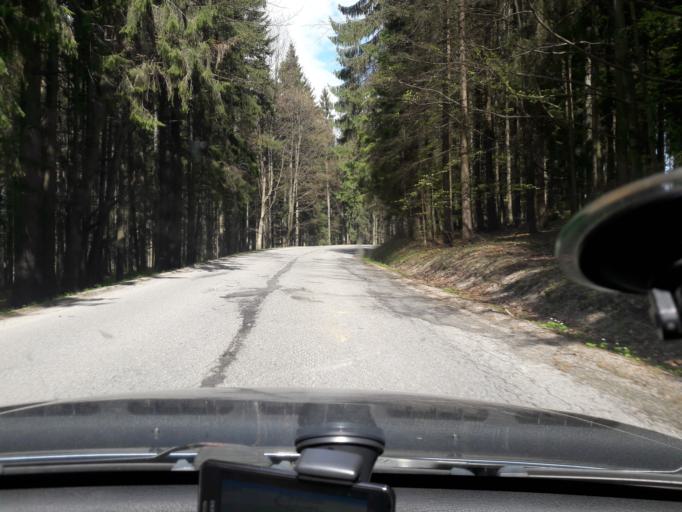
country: SK
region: Banskobystricky
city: Cierny Balog
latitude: 48.6441
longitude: 19.6421
